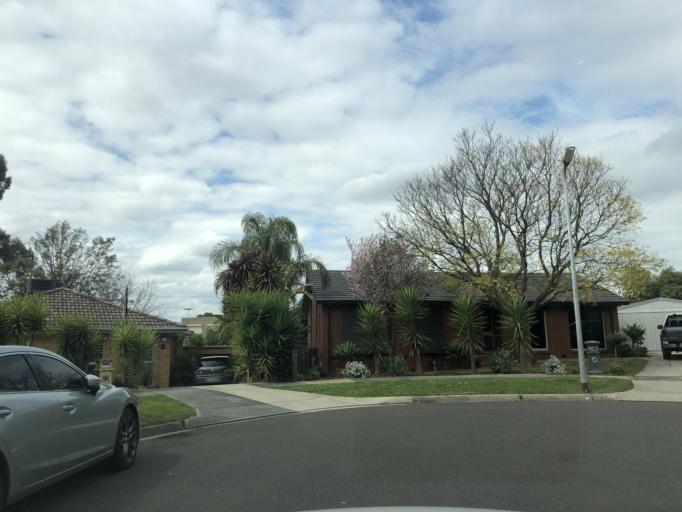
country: AU
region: Victoria
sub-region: Greater Dandenong
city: Noble Park North
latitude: -37.9365
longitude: 145.2029
